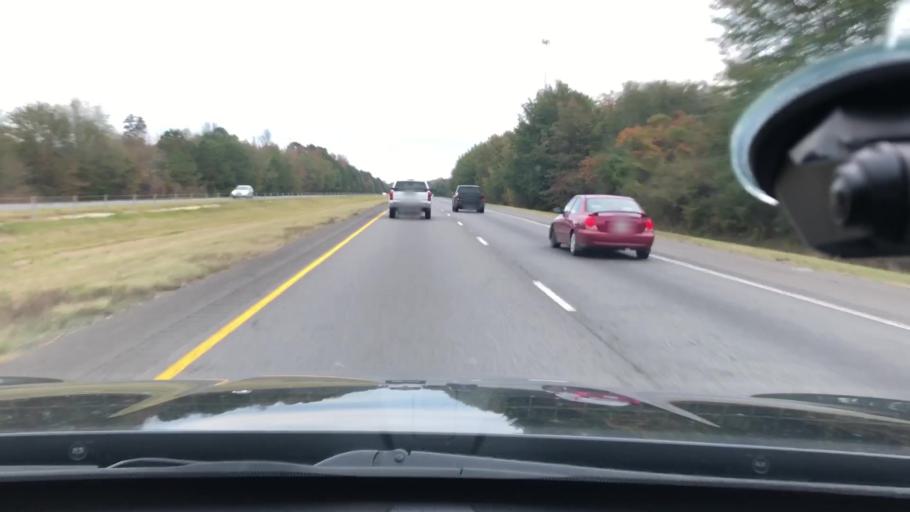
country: US
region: Arkansas
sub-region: Clark County
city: Gurdon
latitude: 34.0156
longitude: -93.1645
